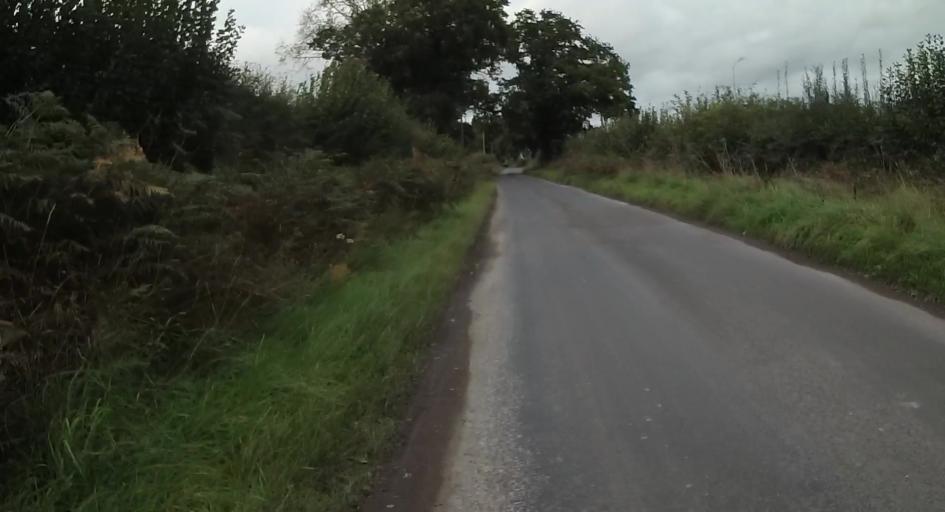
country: GB
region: England
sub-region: Hampshire
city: Kingsley
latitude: 51.1453
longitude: -0.9208
